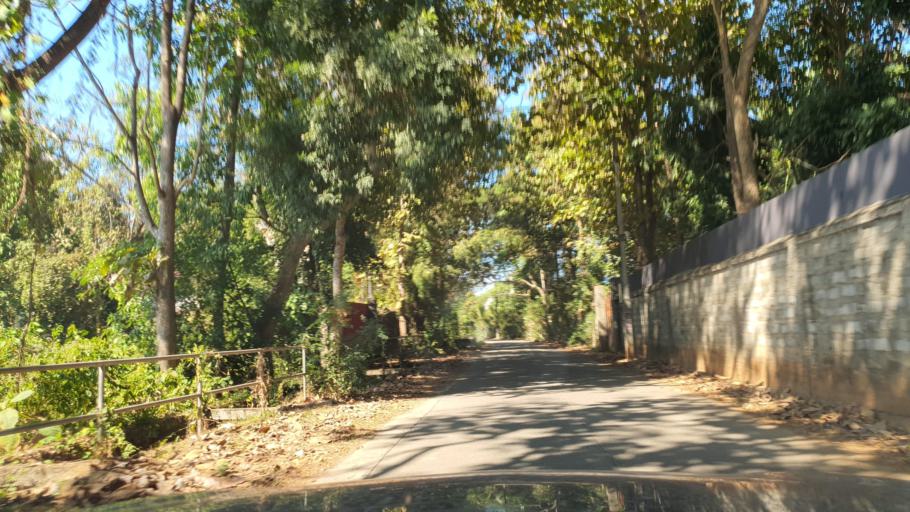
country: TH
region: Chiang Mai
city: Hang Dong
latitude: 18.6798
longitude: 98.9263
